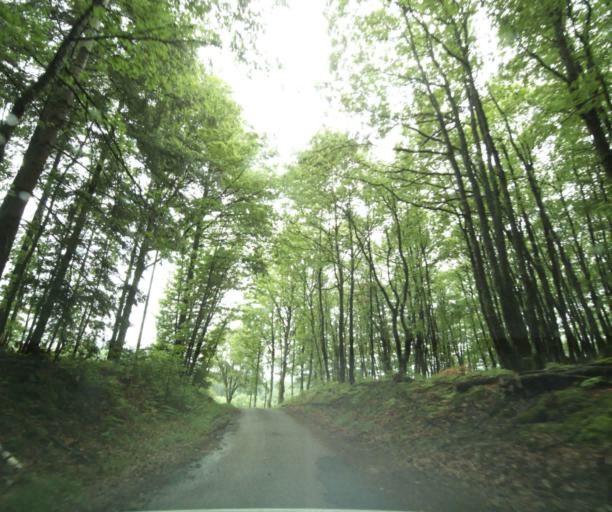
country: FR
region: Bourgogne
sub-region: Departement de Saone-et-Loire
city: Matour
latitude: 46.4428
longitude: 4.4666
